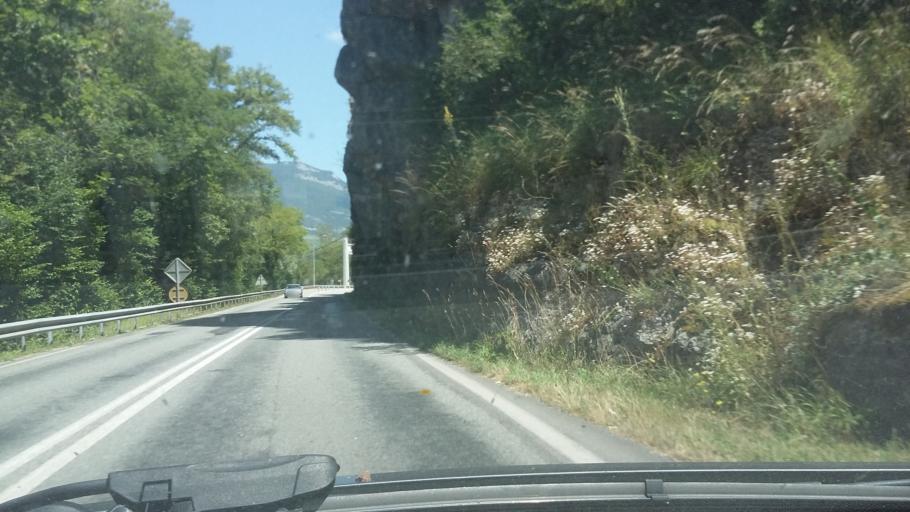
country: FR
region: Rhone-Alpes
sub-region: Departement de la Savoie
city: Yenne
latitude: 45.7047
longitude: 5.7483
